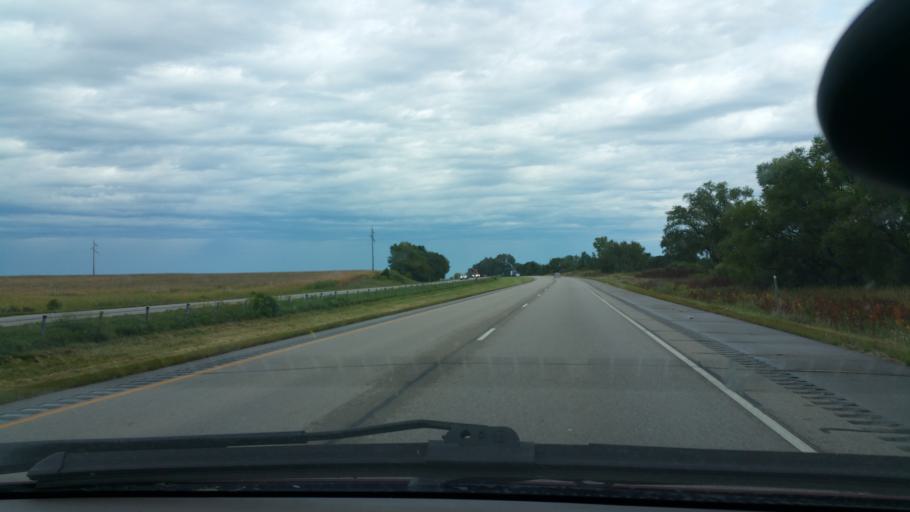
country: US
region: Minnesota
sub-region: Steele County
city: Medford
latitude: 44.2306
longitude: -93.2775
